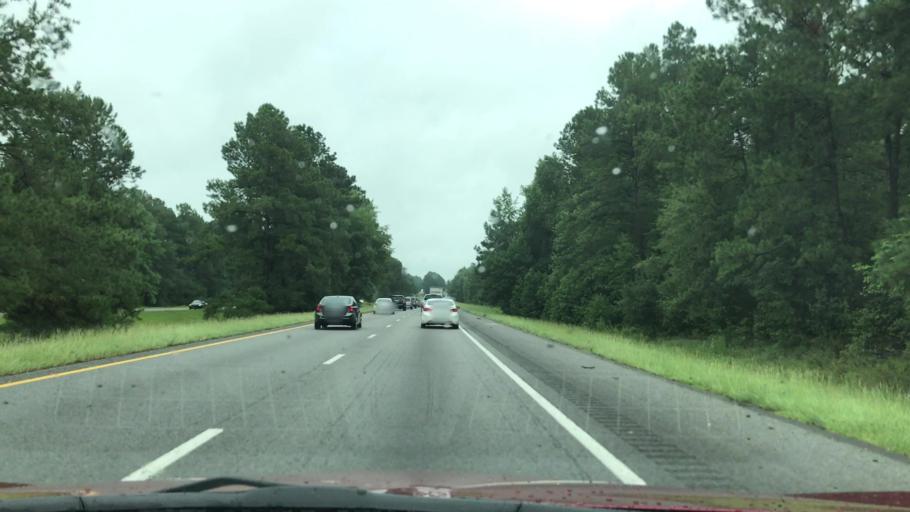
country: US
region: South Carolina
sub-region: Dorchester County
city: Ridgeville
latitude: 33.1703
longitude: -80.3651
